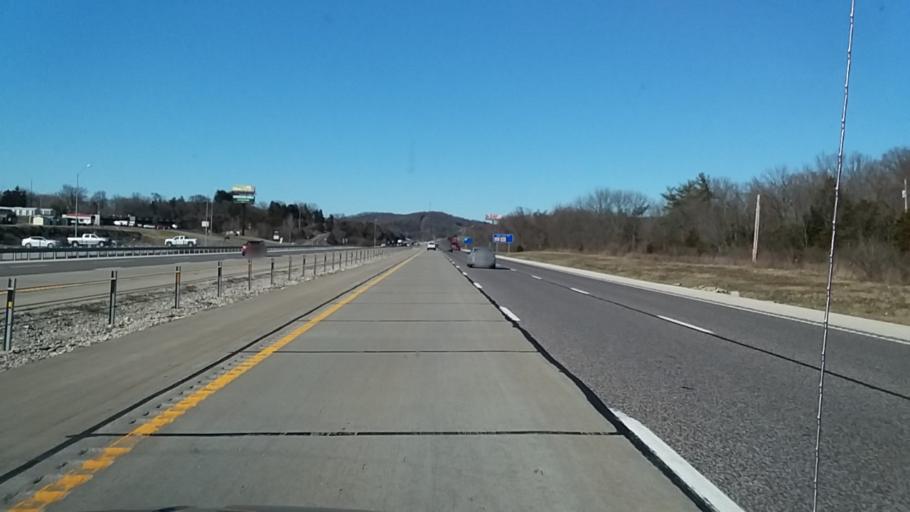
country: US
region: Missouri
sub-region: Jefferson County
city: Barnhart
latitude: 38.3361
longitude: -90.3989
